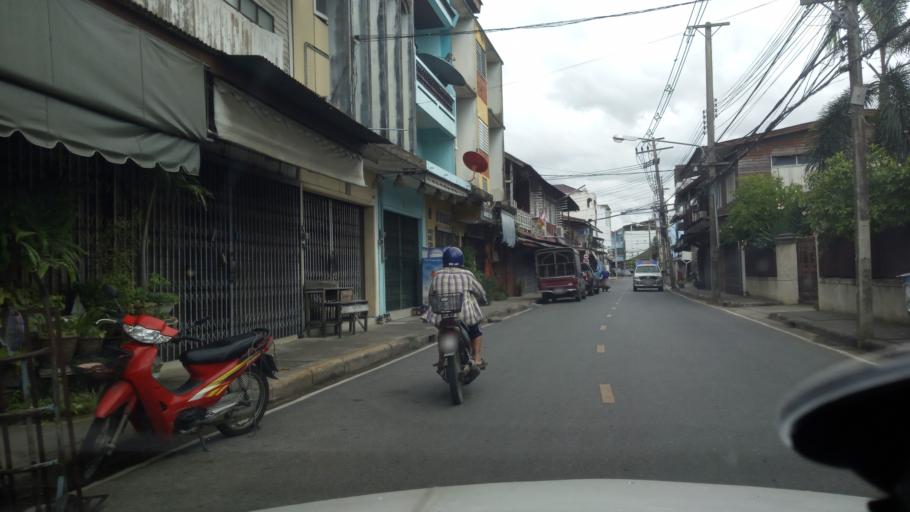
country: TH
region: Chon Buri
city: Phanat Nikhom
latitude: 13.4545
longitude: 101.1802
